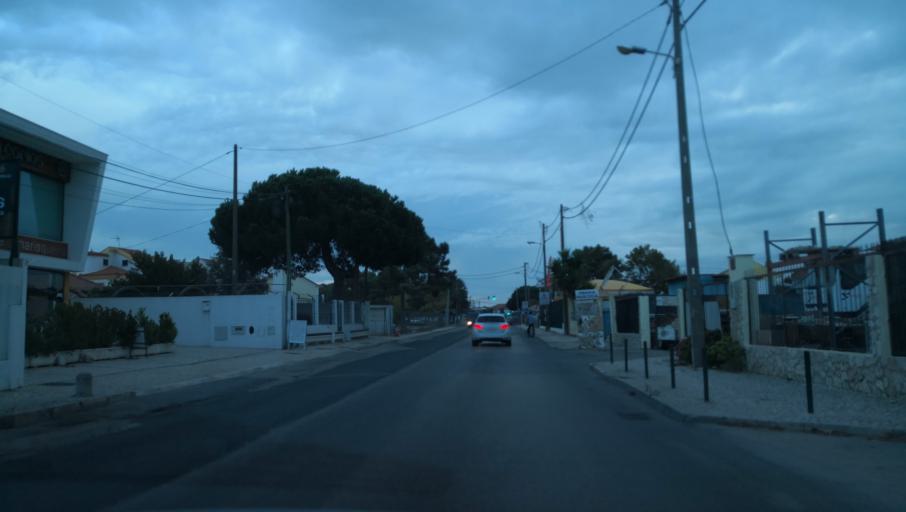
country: PT
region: Setubal
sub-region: Almada
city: Charneca
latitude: 38.6069
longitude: -9.1867
